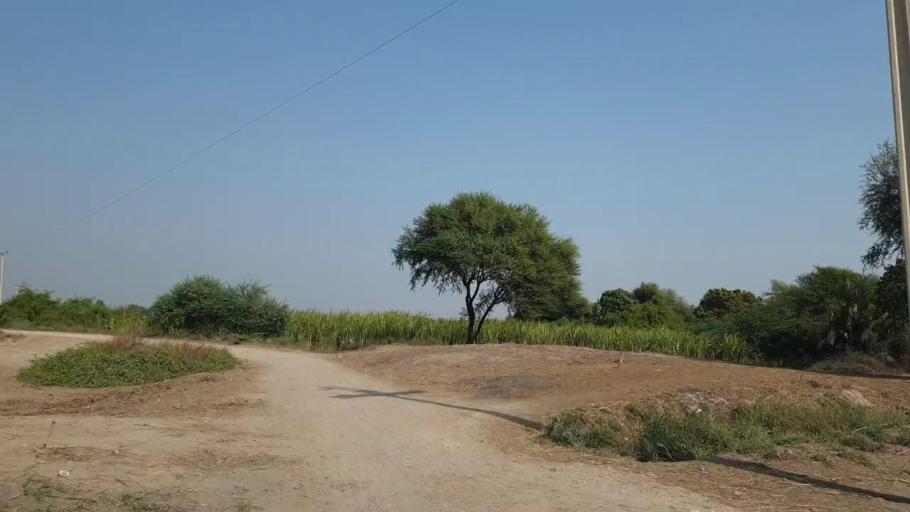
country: PK
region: Sindh
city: Bulri
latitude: 24.9315
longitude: 68.3816
